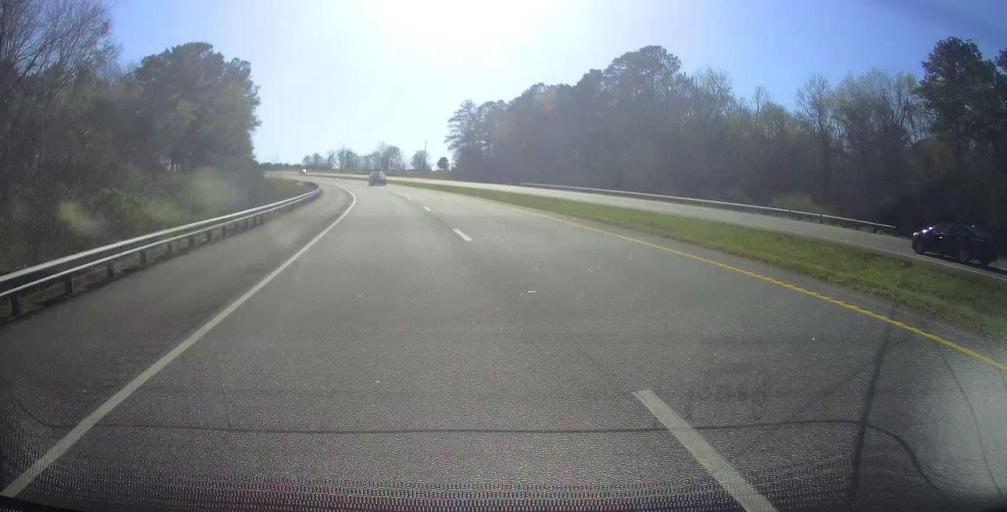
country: US
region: Georgia
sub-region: Peach County
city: Fort Valley
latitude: 32.5679
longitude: -83.9334
